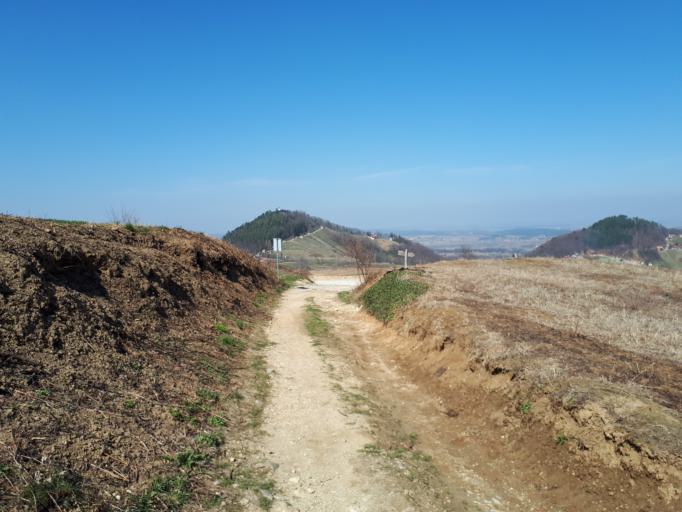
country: HR
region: Varazdinska
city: Ivanec
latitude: 46.1957
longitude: 16.1407
